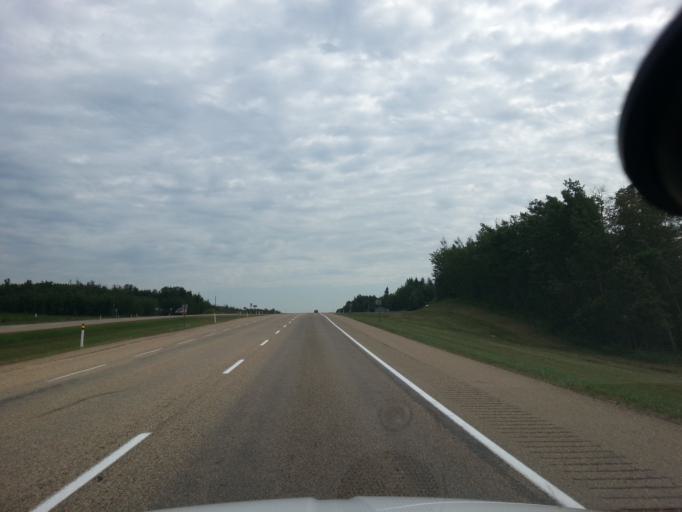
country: CA
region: Alberta
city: Lamont
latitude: 53.5702
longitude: -112.9785
